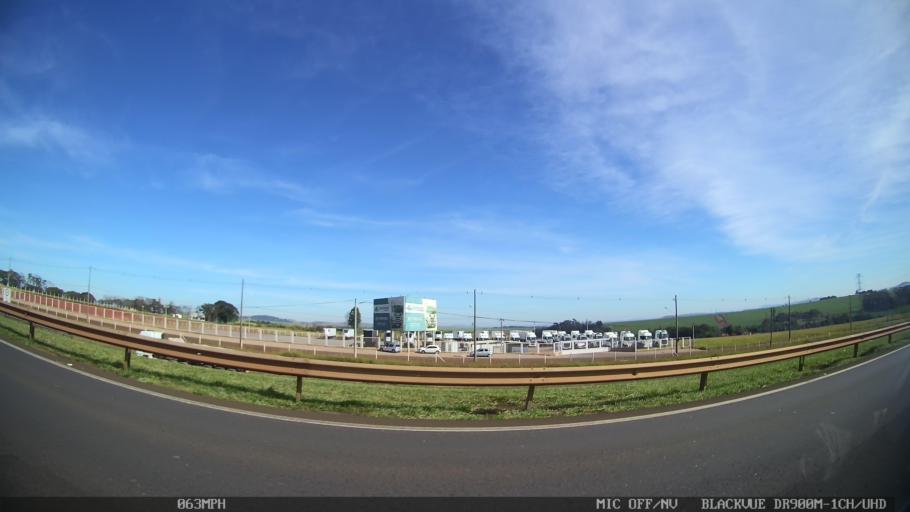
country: BR
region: Sao Paulo
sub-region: Araras
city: Araras
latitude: -22.4029
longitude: -47.3895
